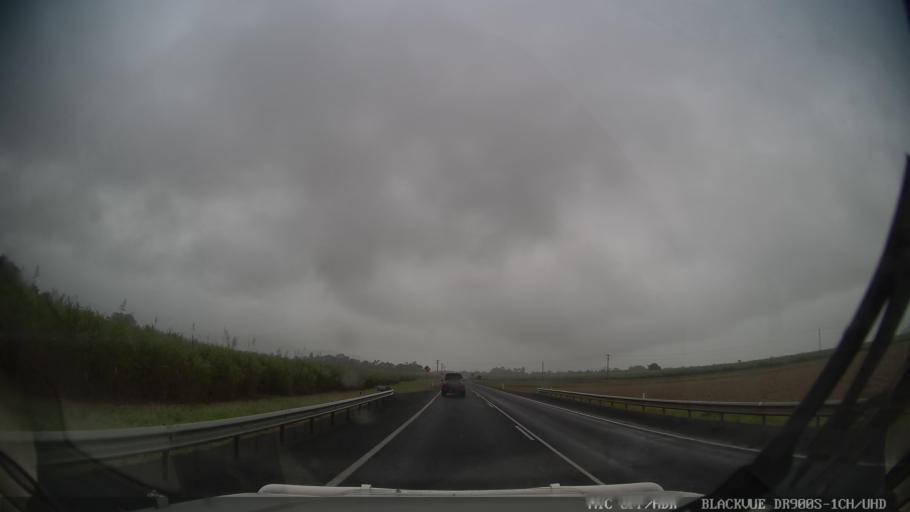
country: AU
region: Queensland
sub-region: Cassowary Coast
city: Innisfail
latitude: -17.6489
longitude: 146.0325
